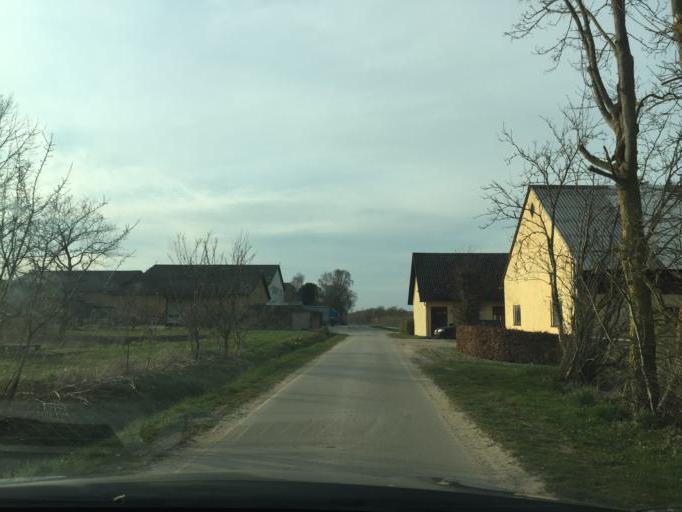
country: DK
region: South Denmark
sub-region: Kerteminde Kommune
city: Langeskov
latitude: 55.3280
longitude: 10.5840
